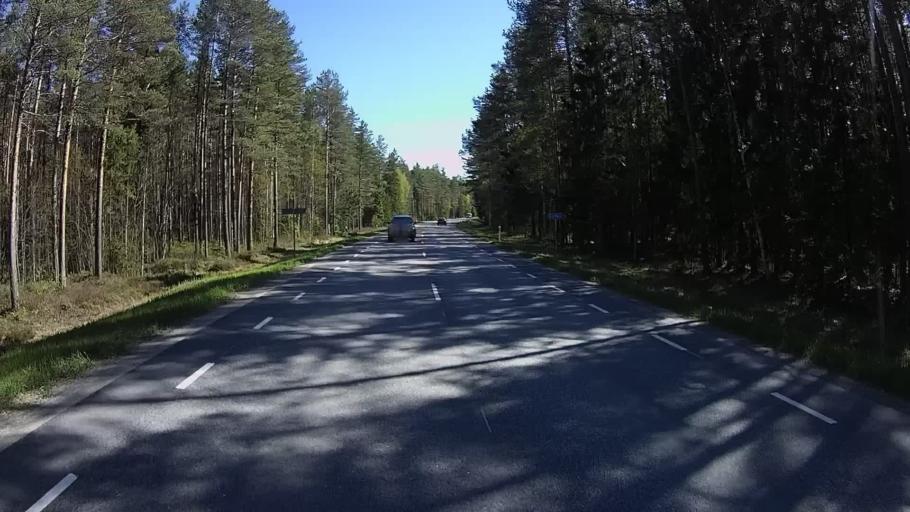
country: EE
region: Harju
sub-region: Loksa linn
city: Loksa
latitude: 59.5465
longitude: 25.7377
